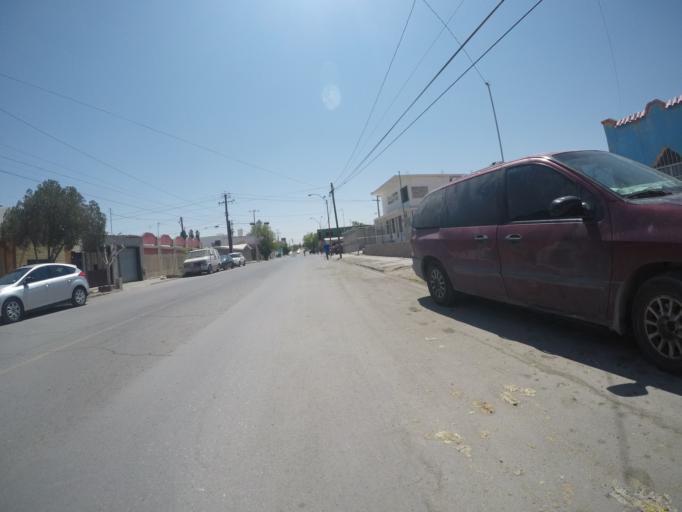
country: MX
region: Chihuahua
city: Ciudad Juarez
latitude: 31.7261
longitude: -106.4830
